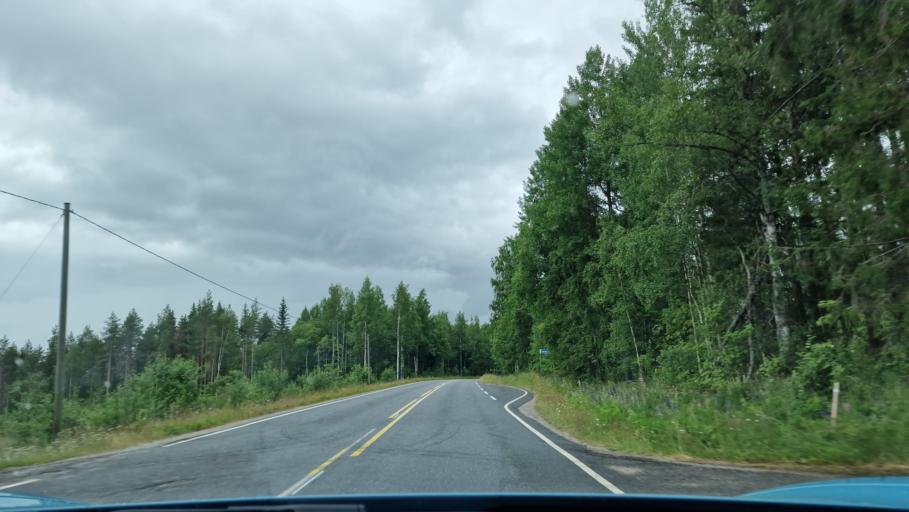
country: FI
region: Southern Ostrobothnia
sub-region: Jaerviseutu
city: Soini
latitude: 62.7604
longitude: 24.3884
